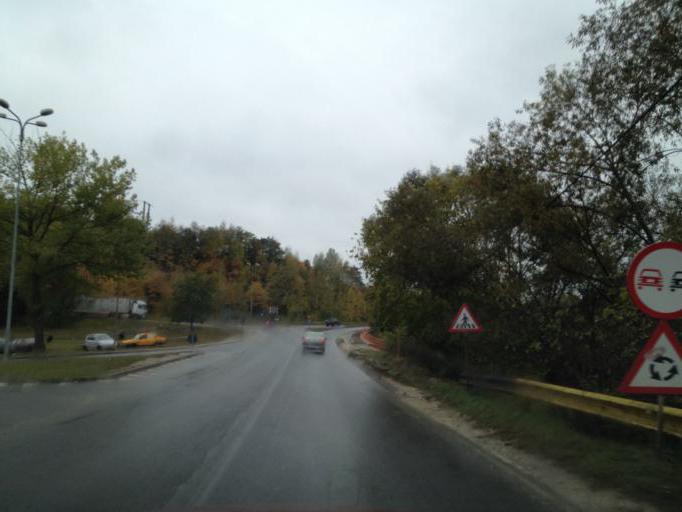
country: RO
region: Arges
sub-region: Comuna Valea Mare-Pravat
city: Valea Mare Pravat
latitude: 45.2957
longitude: 25.1095
